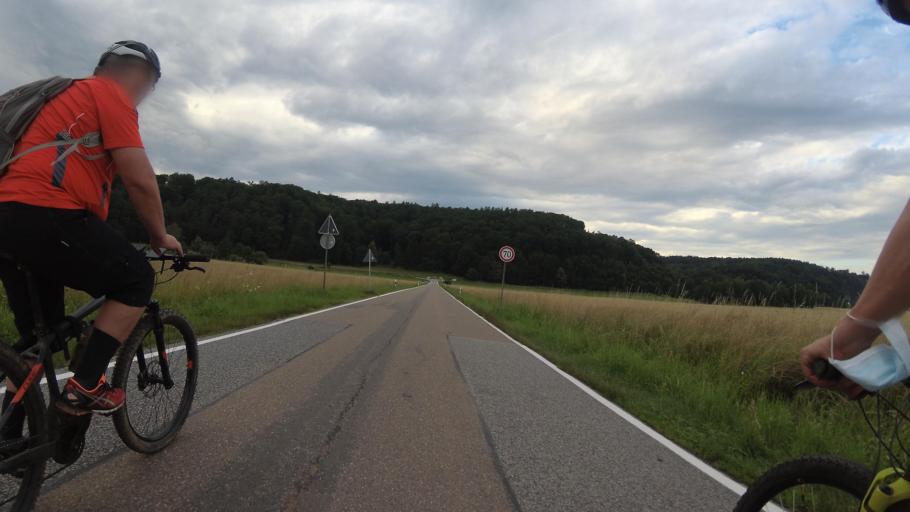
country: DE
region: Saarland
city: Blieskastel
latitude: 49.2713
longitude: 7.3038
